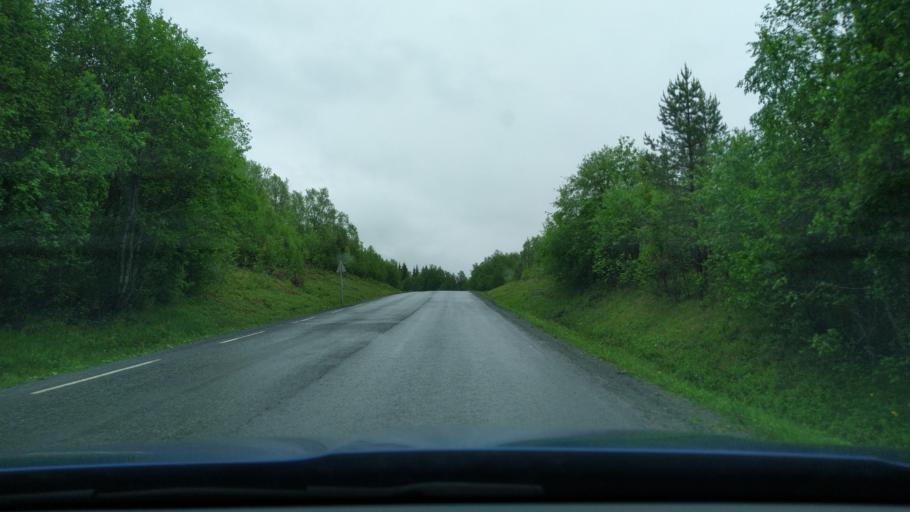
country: NO
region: Troms
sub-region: Dyroy
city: Brostadbotn
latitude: 69.0747
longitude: 17.7105
